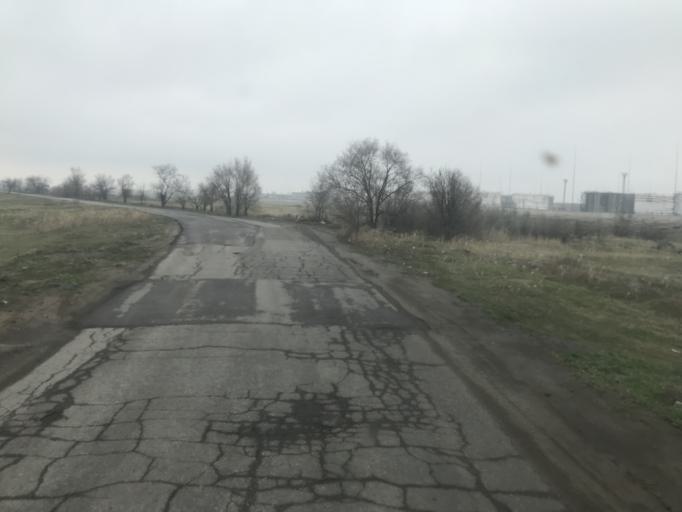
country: RU
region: Volgograd
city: Svetlyy Yar
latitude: 48.4954
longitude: 44.6522
